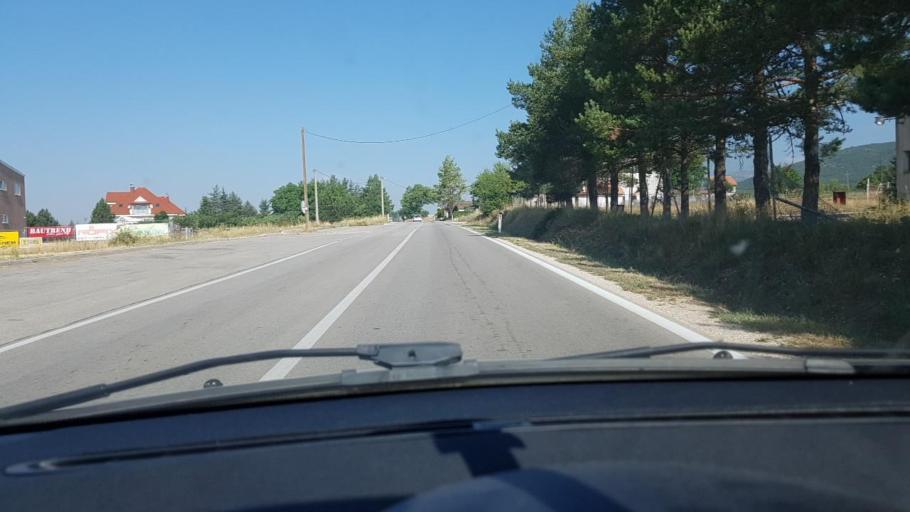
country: BA
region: Federation of Bosnia and Herzegovina
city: Livno
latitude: 43.8431
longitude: 16.9676
